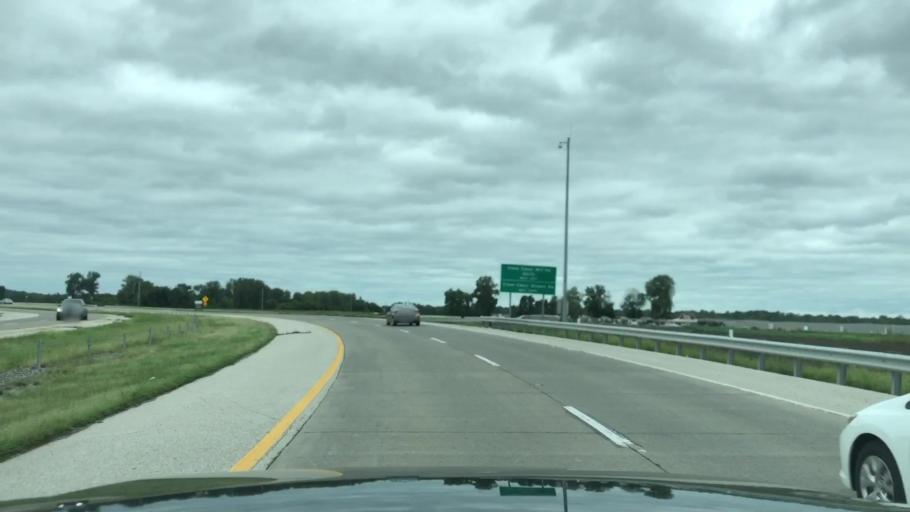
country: US
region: Missouri
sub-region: Saint Charles County
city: Saint Charles
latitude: 38.7274
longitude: -90.4975
